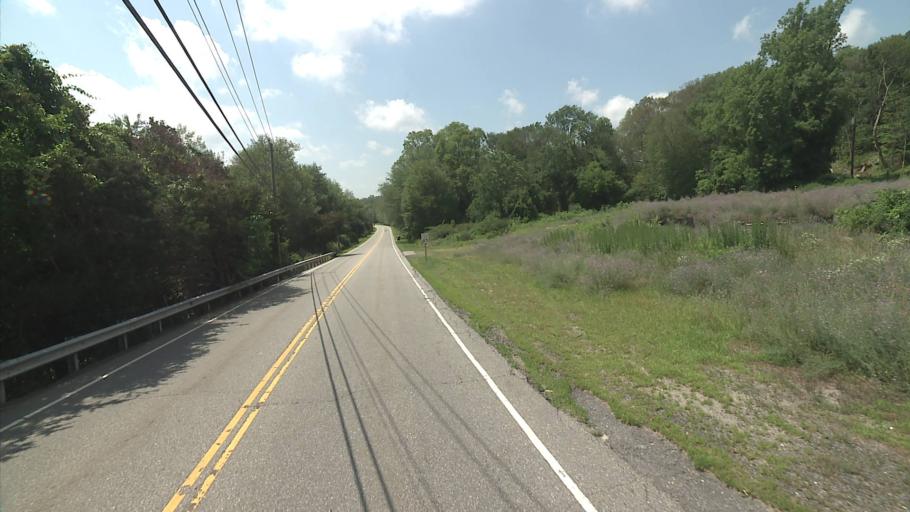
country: US
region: Connecticut
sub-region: New London County
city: Preston City
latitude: 41.5349
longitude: -71.9308
